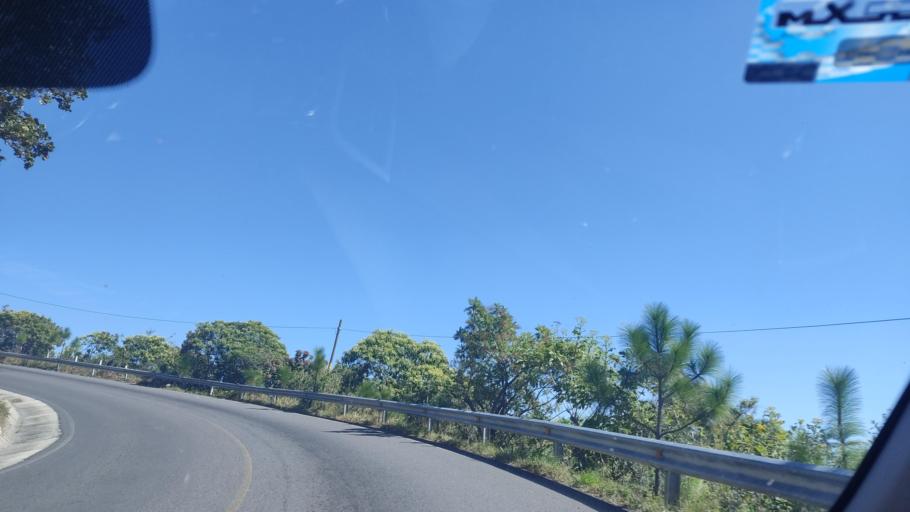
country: MX
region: Nayarit
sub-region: Jala
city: Rosa Blanca
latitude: 21.0981
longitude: -104.3634
